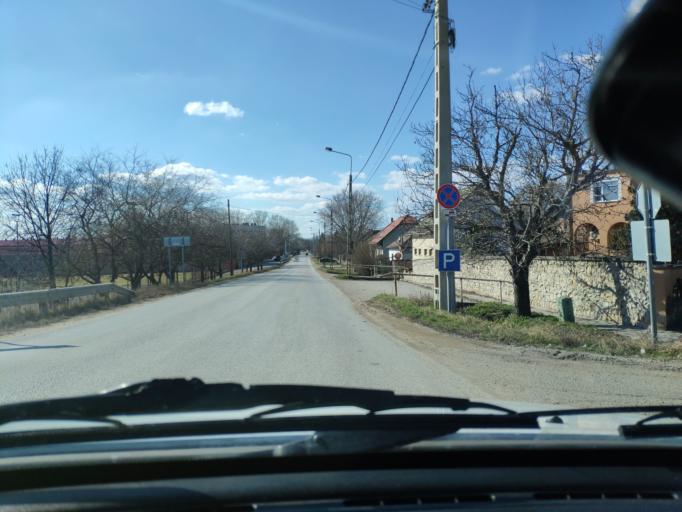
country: HU
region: Pest
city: Ecser
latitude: 47.4388
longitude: 19.3176
